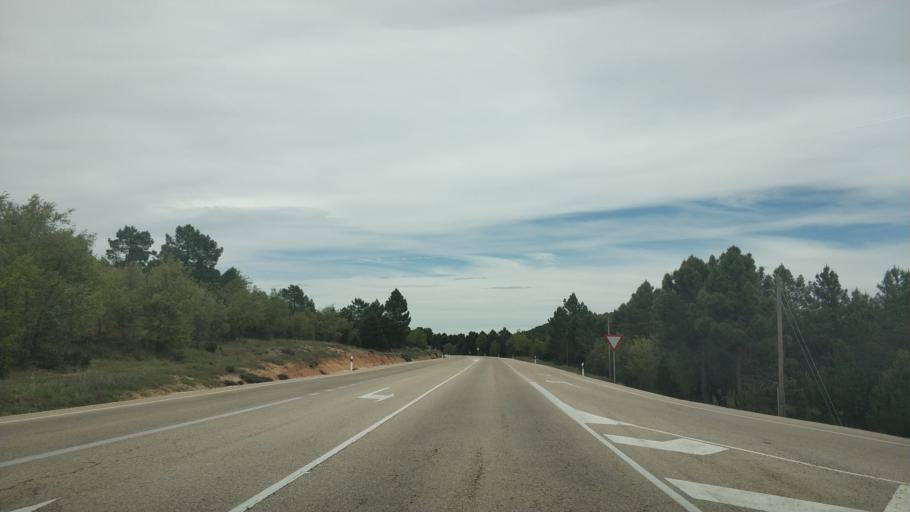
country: ES
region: Castille and Leon
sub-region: Provincia de Soria
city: Bayubas de Abajo
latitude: 41.5116
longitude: -2.9233
